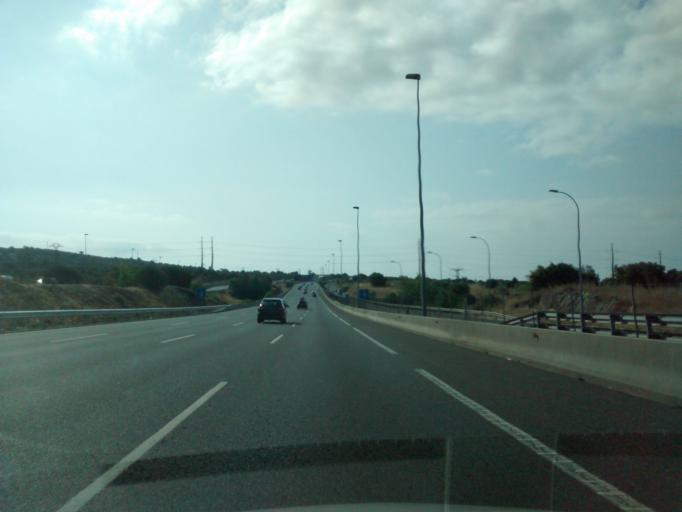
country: ES
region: Madrid
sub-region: Provincia de Madrid
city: Collado-Villalba
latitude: 40.6206
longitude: -3.9872
